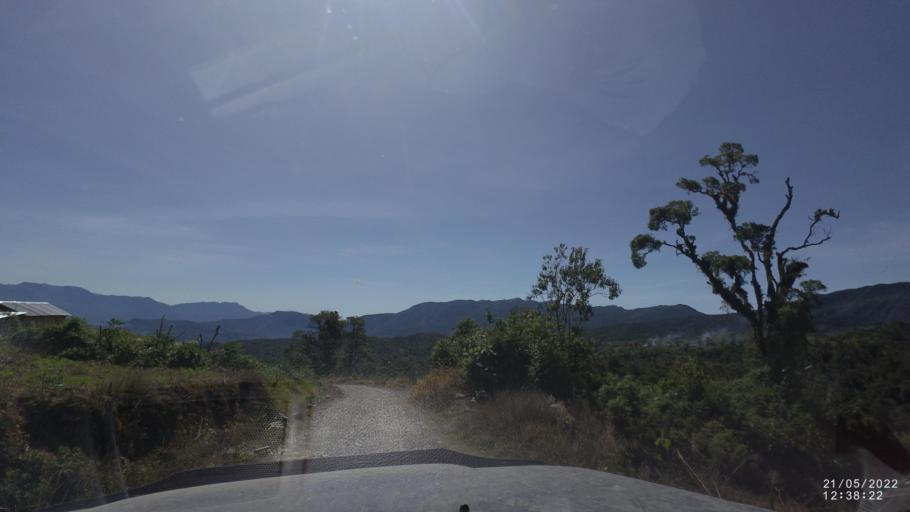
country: BO
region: Cochabamba
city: Colomi
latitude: -17.2007
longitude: -65.9200
